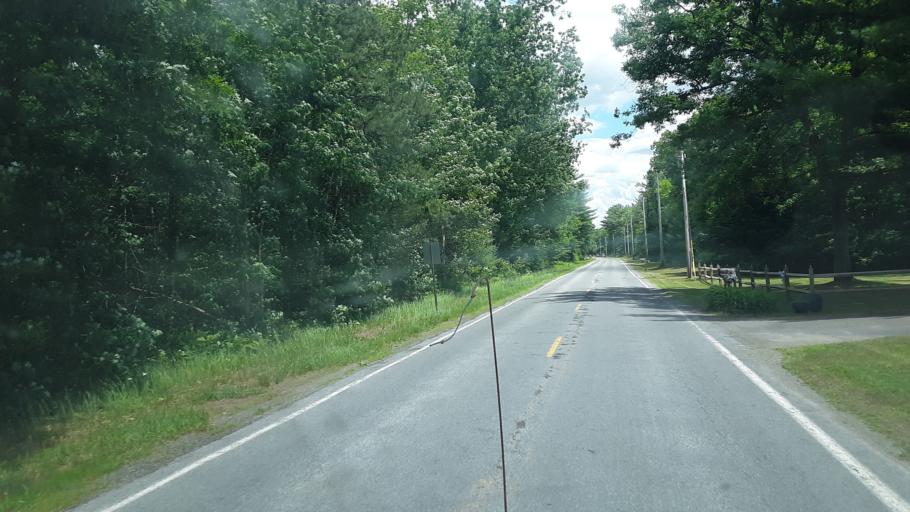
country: US
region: New York
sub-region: Oneida County
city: Rome
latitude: 43.2631
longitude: -75.5735
